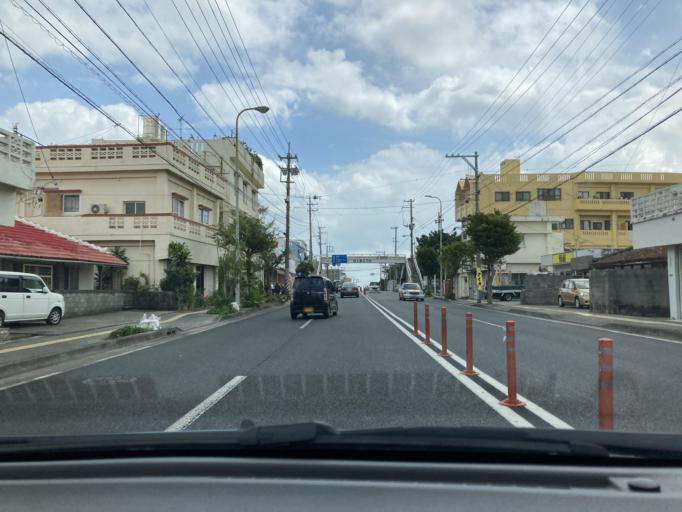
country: JP
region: Okinawa
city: Okinawa
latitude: 26.3340
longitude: 127.8189
